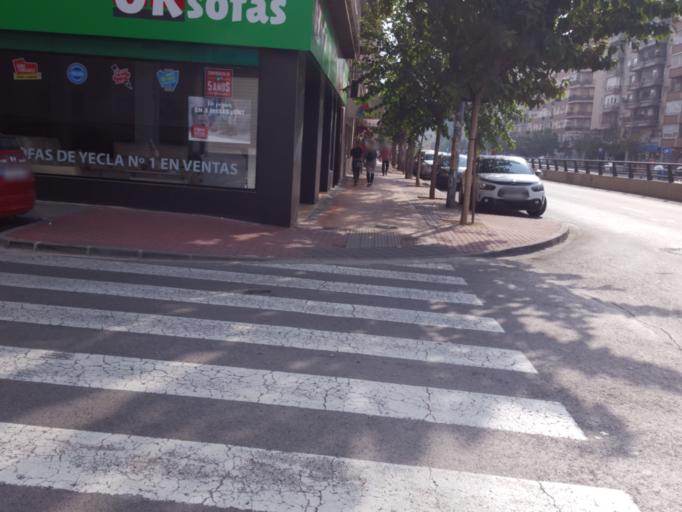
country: ES
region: Murcia
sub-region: Murcia
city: Murcia
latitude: 37.9931
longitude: -1.1405
